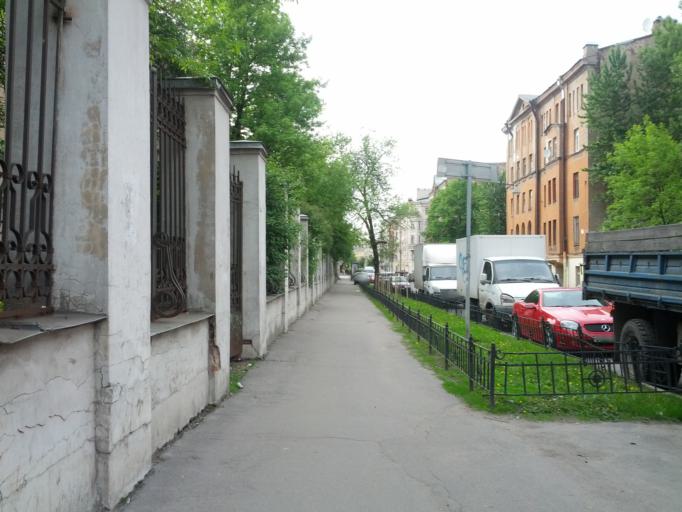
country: RU
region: St.-Petersburg
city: Centralniy
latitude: 59.9202
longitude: 30.3468
